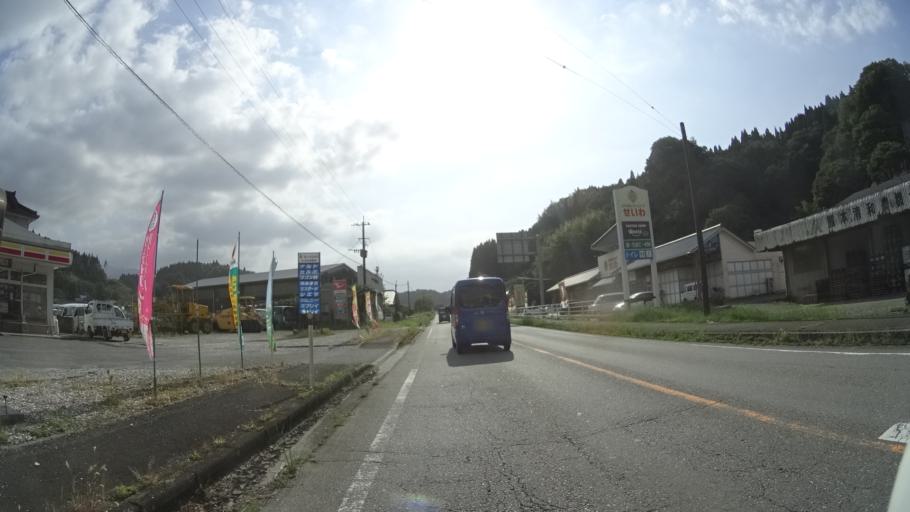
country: JP
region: Kumamoto
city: Aso
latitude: 32.6888
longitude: 131.0865
